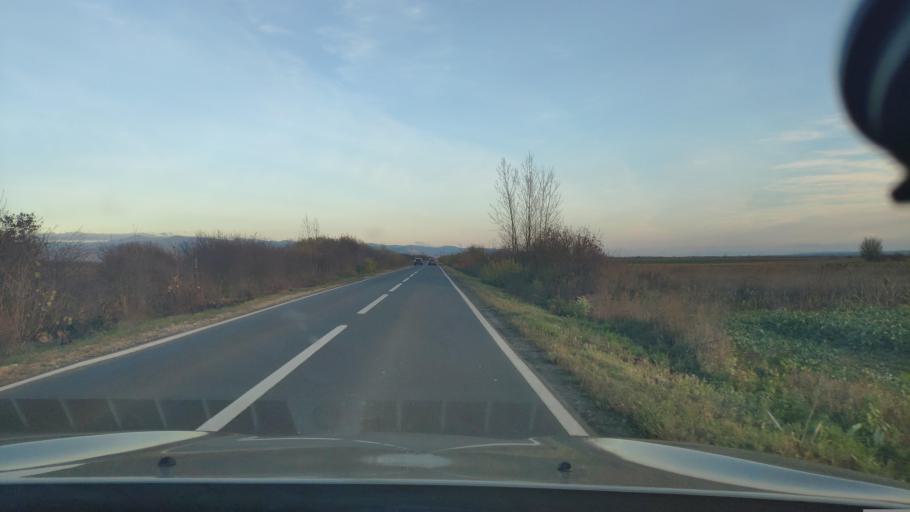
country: RO
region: Satu Mare
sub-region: Comuna Mediesu Aurit
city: Mediesu Aurit
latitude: 47.7688
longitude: 23.1526
